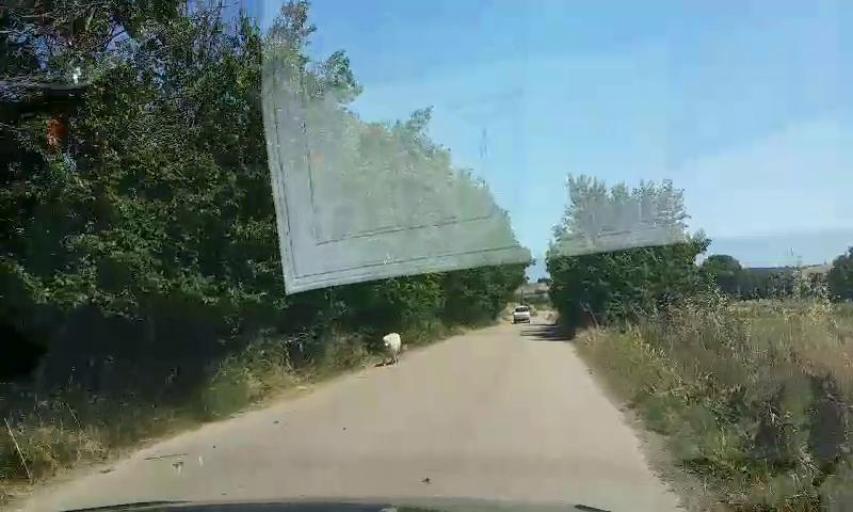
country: IT
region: Molise
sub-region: Provincia di Campobasso
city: Guglionesi
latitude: 41.9407
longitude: 14.8961
